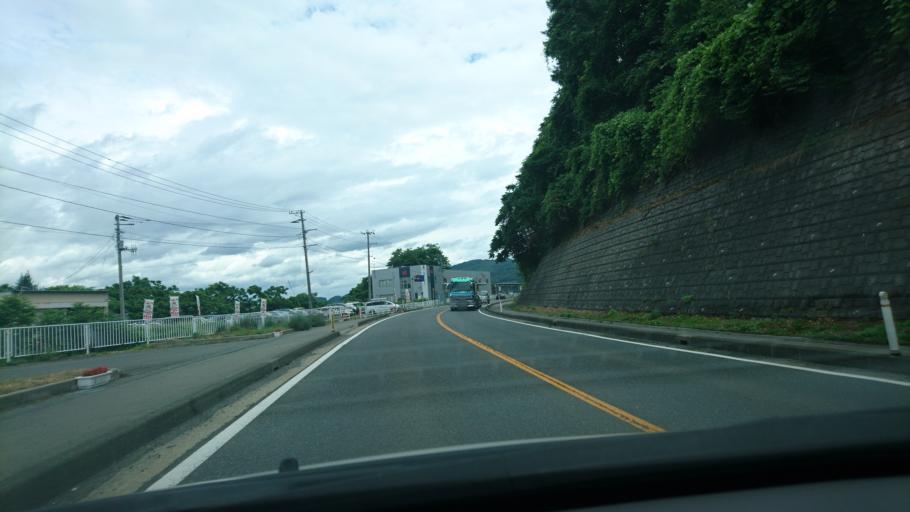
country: JP
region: Iwate
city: Morioka-shi
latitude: 39.6338
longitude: 141.1844
